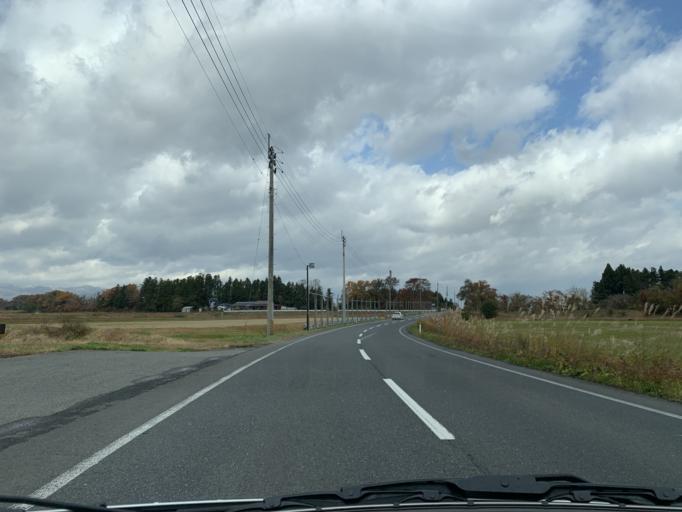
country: JP
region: Iwate
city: Mizusawa
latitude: 39.0802
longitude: 141.0515
